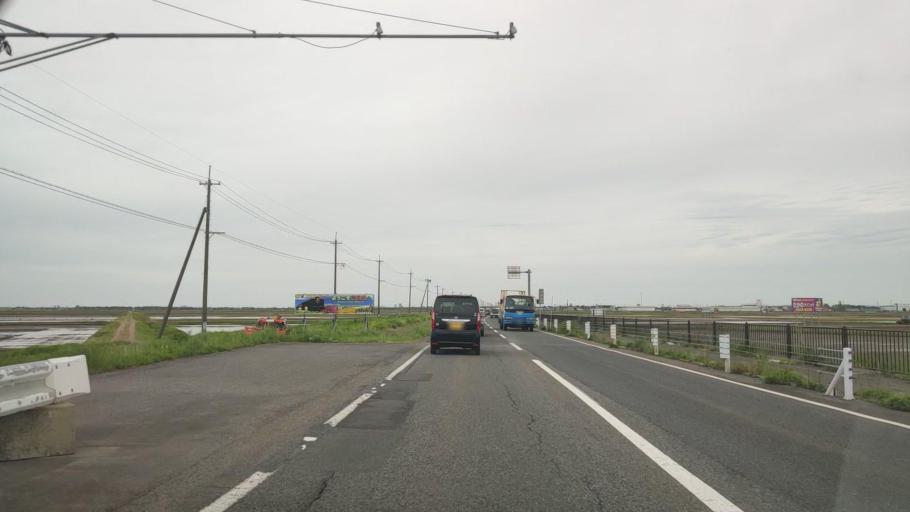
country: JP
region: Niigata
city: Niitsu-honcho
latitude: 37.8044
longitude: 139.1022
